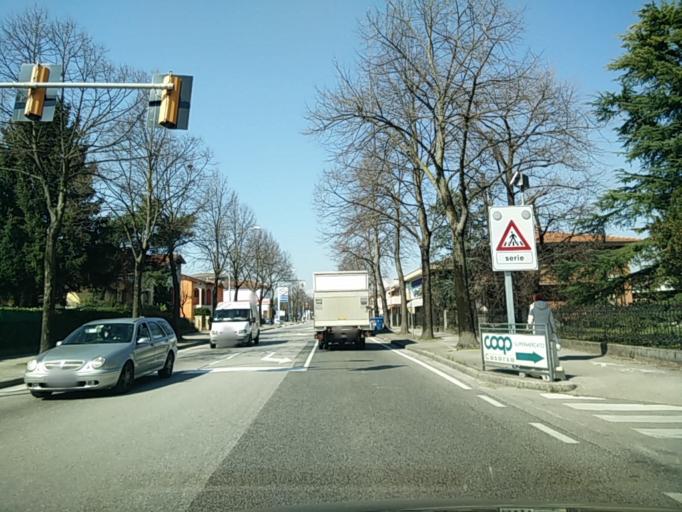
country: IT
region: Friuli Venezia Giulia
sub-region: Provincia di Pordenone
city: Casarsa della Delizia
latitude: 45.9558
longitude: 12.8384
